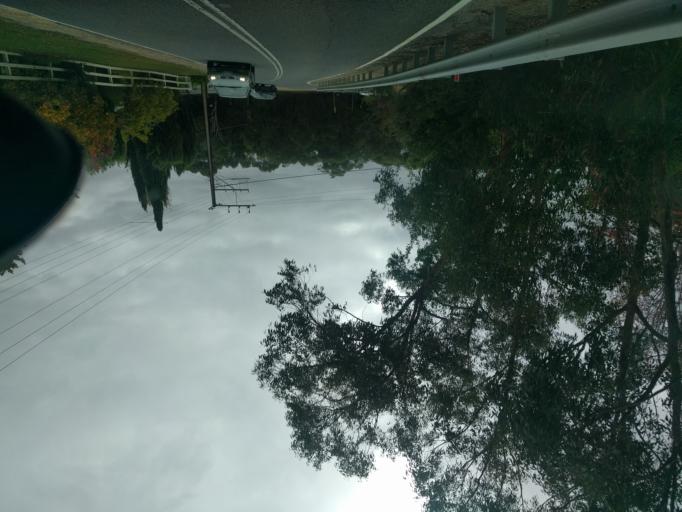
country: AU
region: South Australia
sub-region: Adelaide Hills
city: Stirling
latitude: -35.0498
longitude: 138.7587
